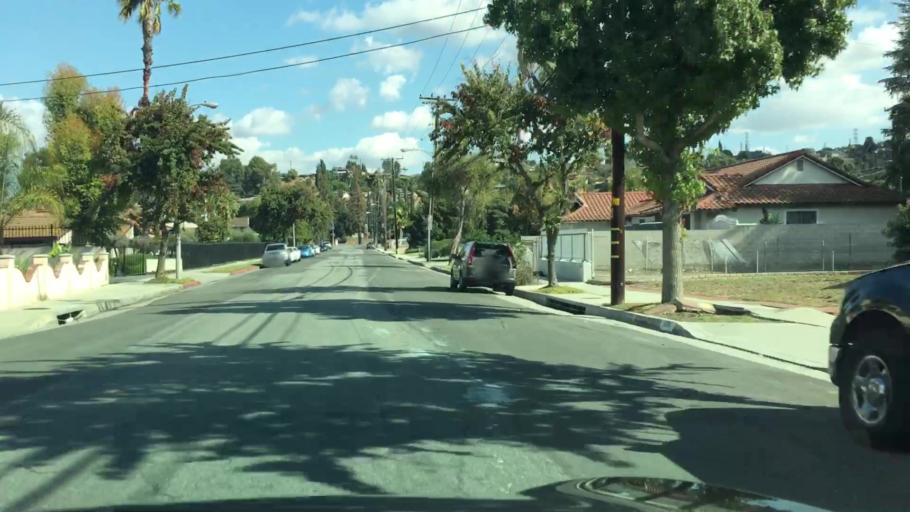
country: US
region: California
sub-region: Los Angeles County
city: Hacienda Heights
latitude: 33.9906
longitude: -117.9729
